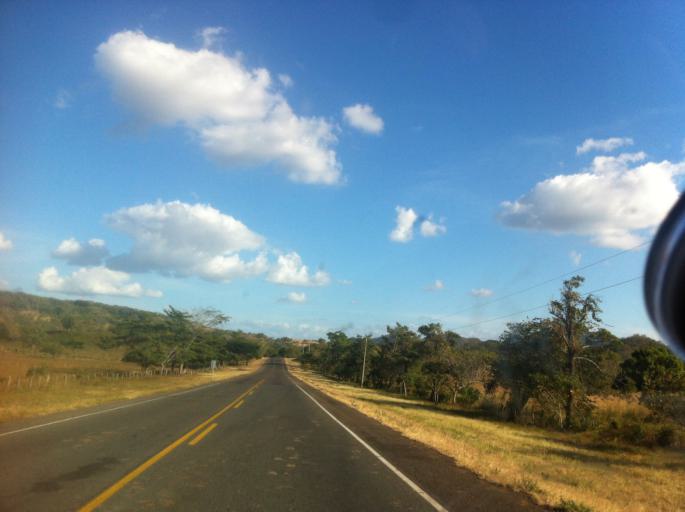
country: NI
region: Chontales
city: Acoyapa
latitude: 11.8840
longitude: -85.0978
